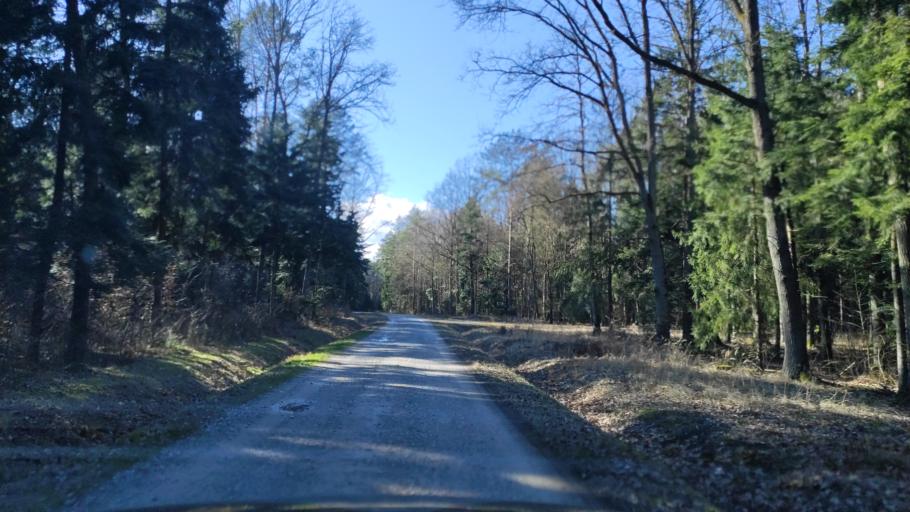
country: PL
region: Masovian Voivodeship
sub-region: Powiat radomski
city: Jastrzebia
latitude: 51.4744
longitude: 21.2712
